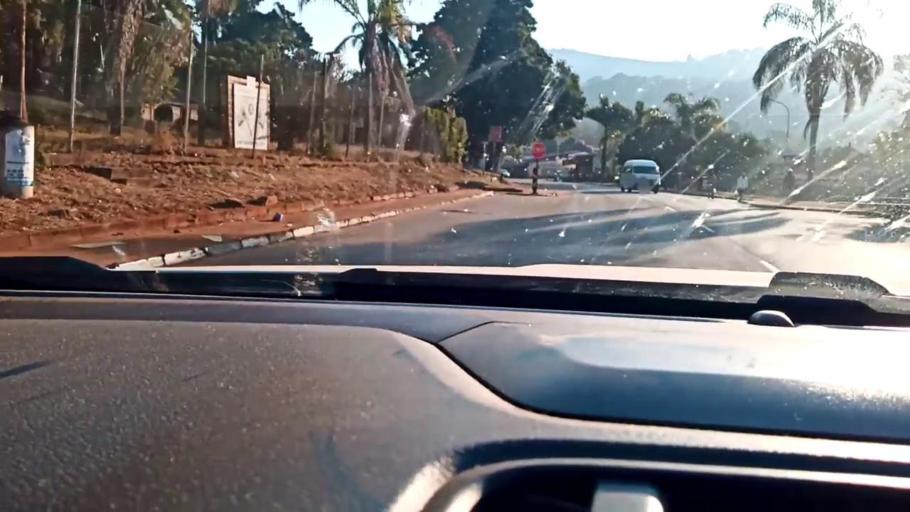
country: ZA
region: Limpopo
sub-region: Mopani District Municipality
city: Duiwelskloof
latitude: -23.6952
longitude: 30.1446
